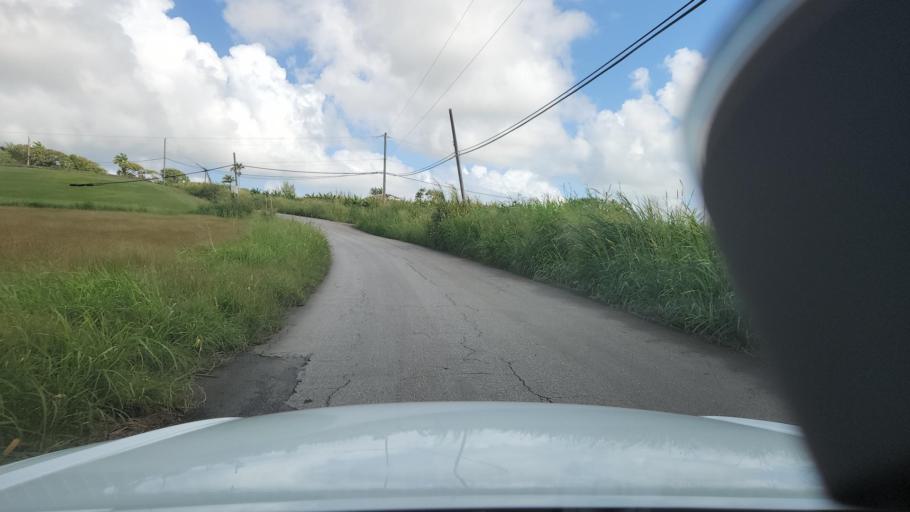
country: BB
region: Saint Thomas
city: Welchman Hall
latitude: 13.1558
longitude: -59.5514
